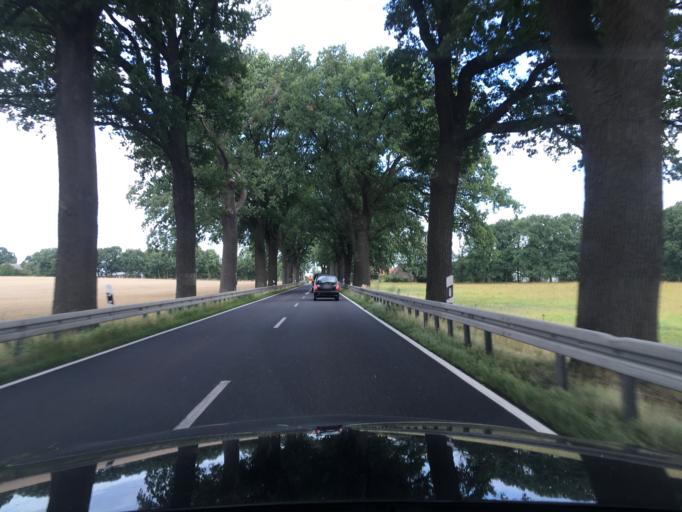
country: DE
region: Brandenburg
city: Gransee
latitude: 52.9739
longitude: 13.1521
